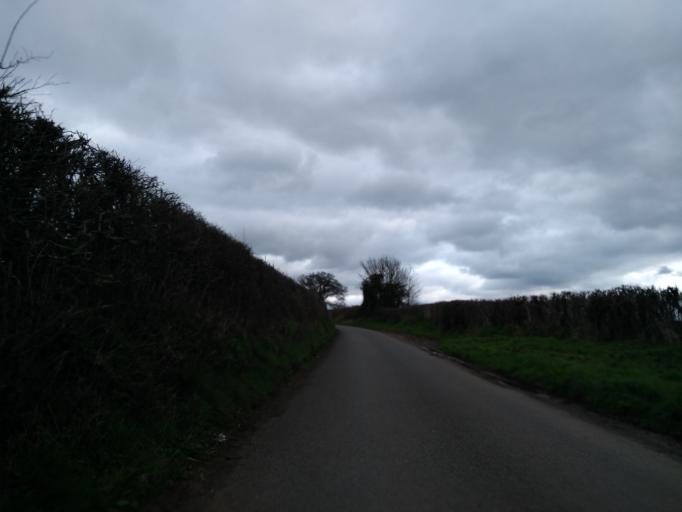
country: GB
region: England
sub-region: Devon
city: Crediton
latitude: 50.7872
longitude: -3.6171
